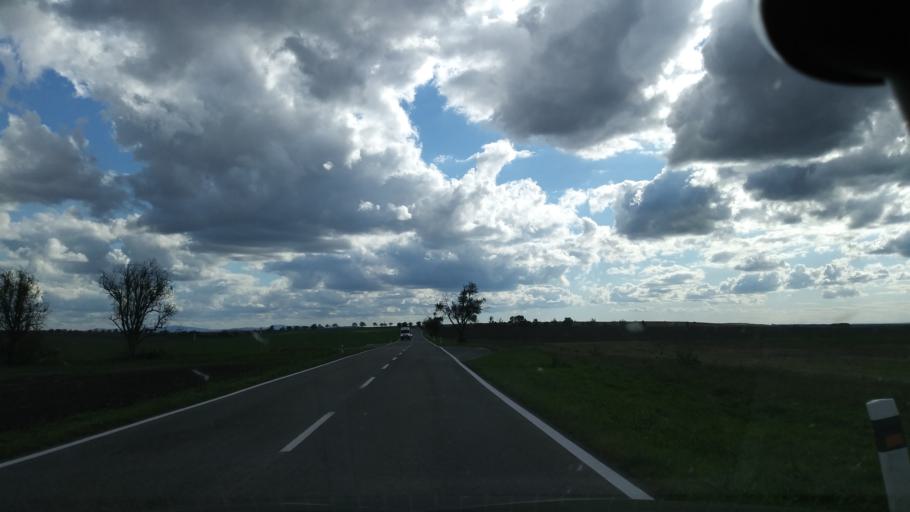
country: SK
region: Trnavsky
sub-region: Okres Skalica
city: Holic
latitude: 48.7715
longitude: 17.1739
